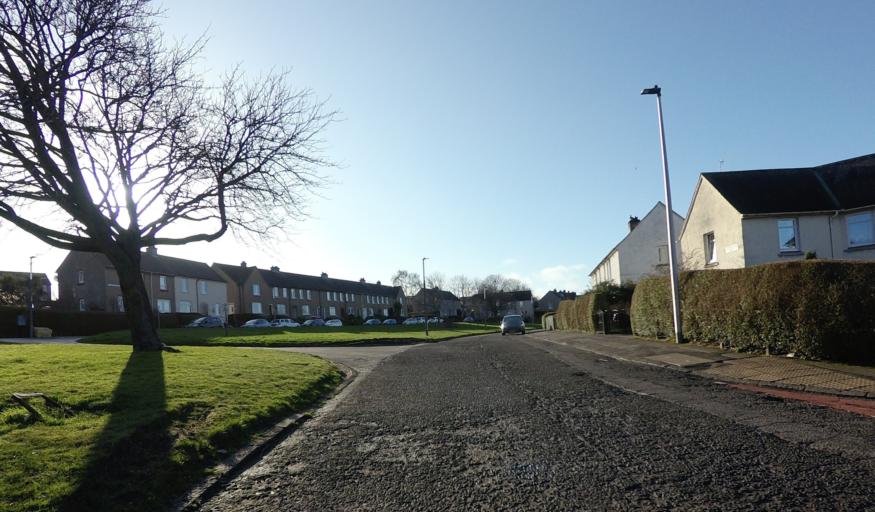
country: GB
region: Scotland
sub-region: Edinburgh
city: Colinton
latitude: 55.9609
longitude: -3.2840
